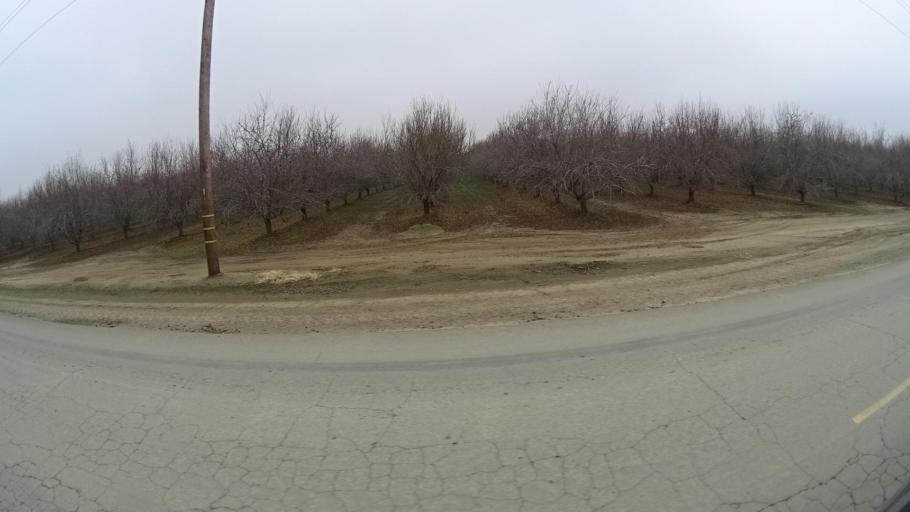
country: US
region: California
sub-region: Kern County
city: Greenfield
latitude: 35.2379
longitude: -119.0522
